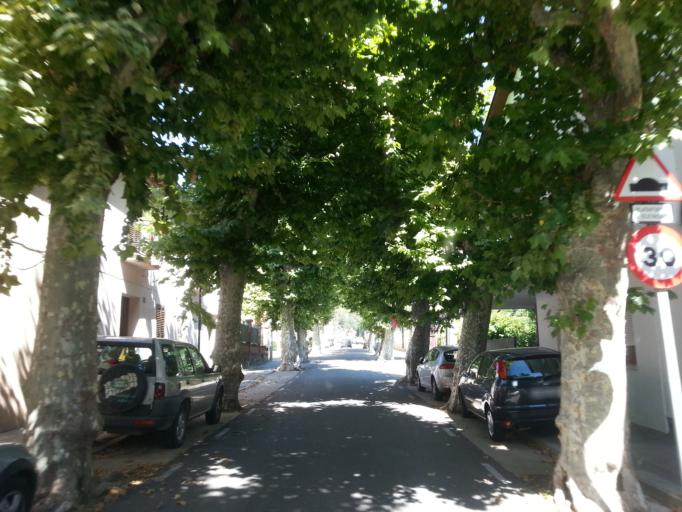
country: ES
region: Catalonia
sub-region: Provincia de Barcelona
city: Campins
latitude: 41.7312
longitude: 2.5033
